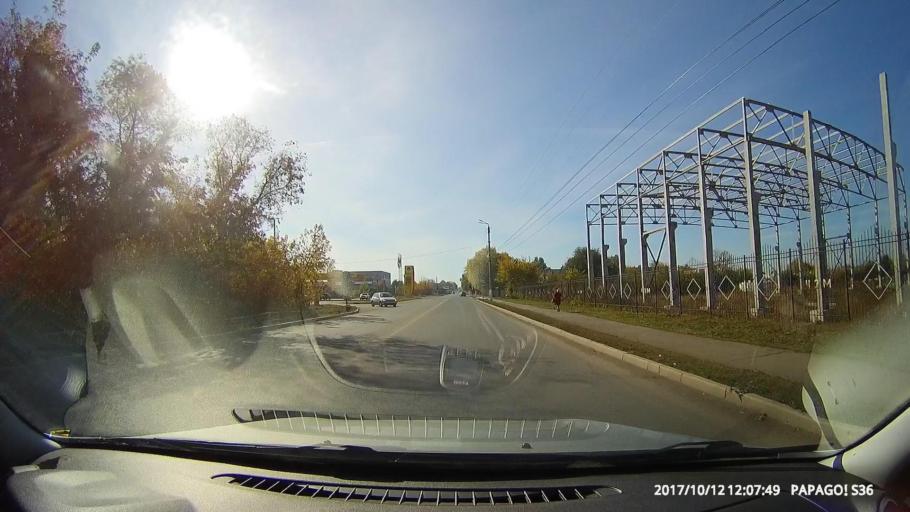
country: RU
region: Samara
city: Chapayevsk
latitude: 52.9654
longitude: 49.6995
